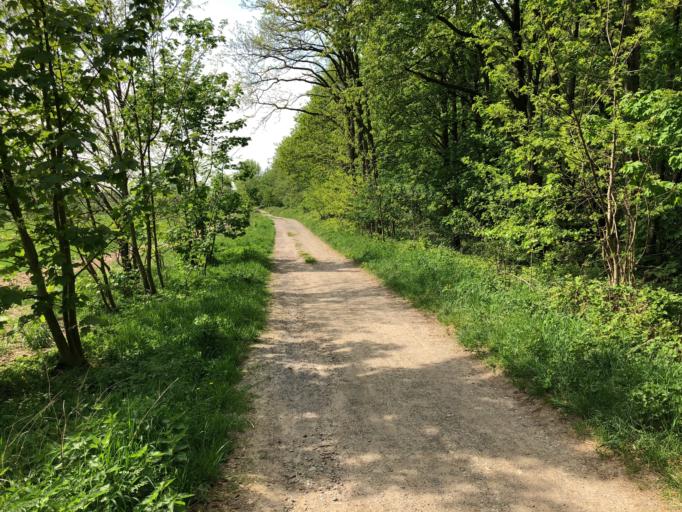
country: DE
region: North Rhine-Westphalia
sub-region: Regierungsbezirk Dusseldorf
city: Muelheim (Ruhr)
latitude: 51.3789
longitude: 6.8866
